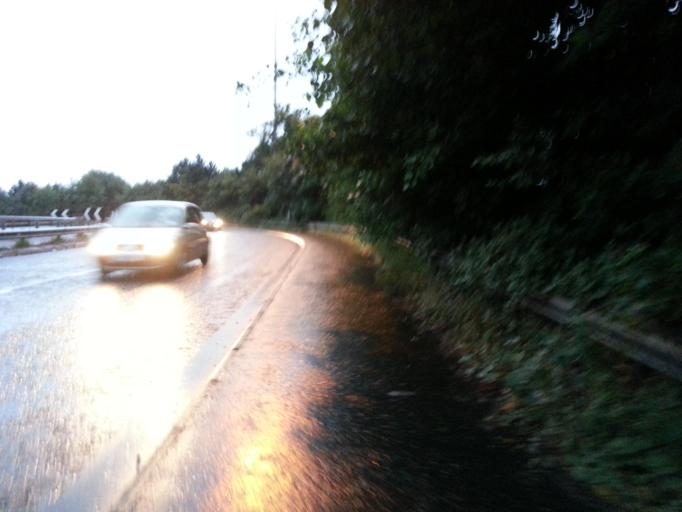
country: GB
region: Northern Ireland
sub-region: Newtownabbey District
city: Newtownabbey
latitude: 54.6306
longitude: -5.9219
